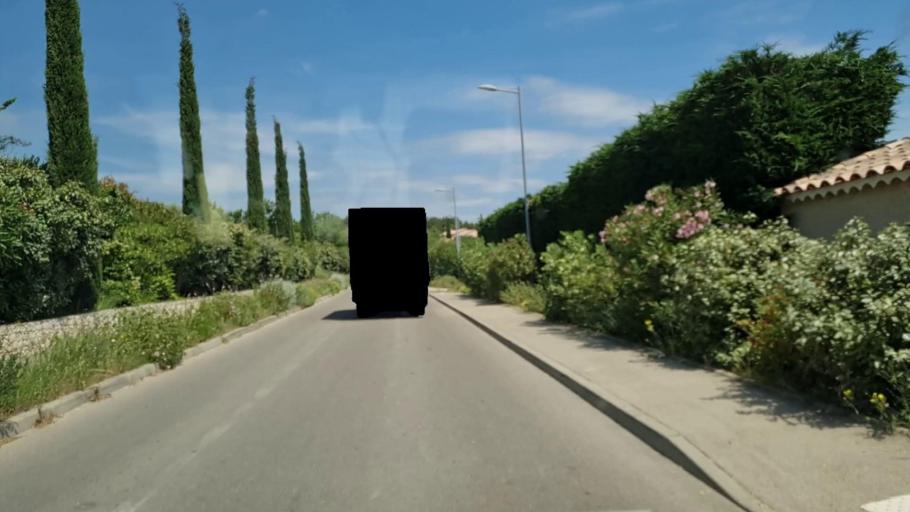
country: FR
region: Languedoc-Roussillon
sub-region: Departement du Gard
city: Cabrieres
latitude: 43.8984
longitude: 4.4730
